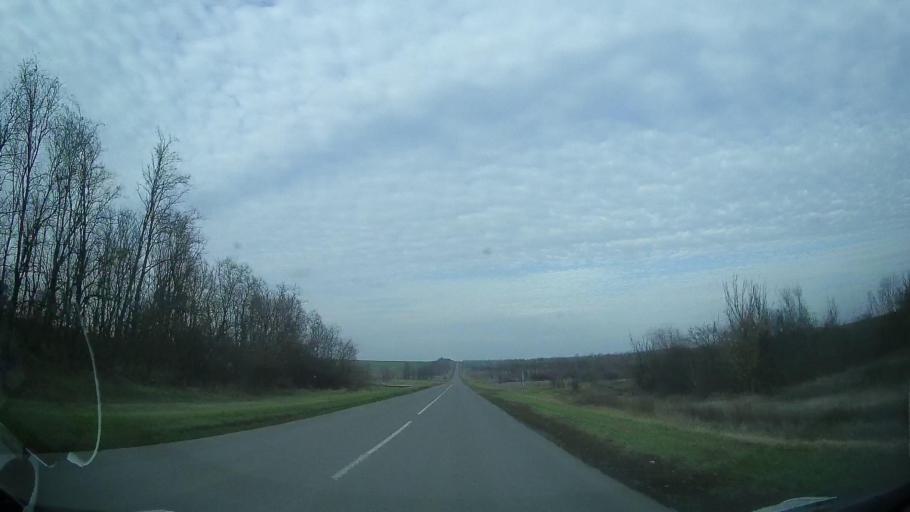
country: RU
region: Rostov
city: Zernograd
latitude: 46.8941
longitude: 40.3389
